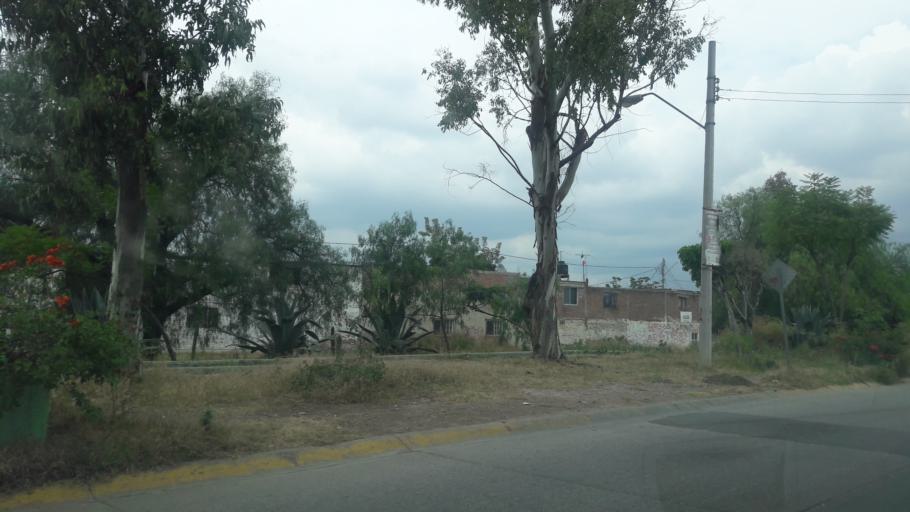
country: MX
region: Guanajuato
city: Leon
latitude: 21.1787
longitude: -101.6691
